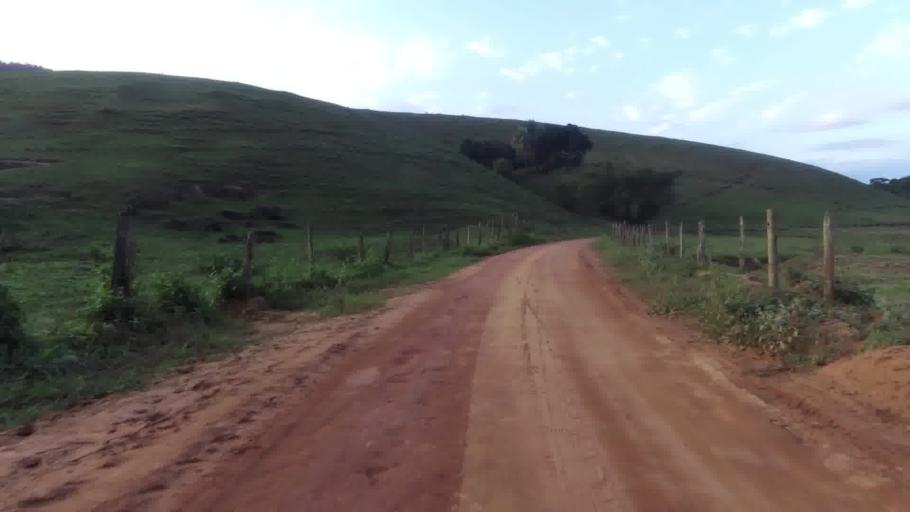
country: BR
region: Espirito Santo
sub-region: Alfredo Chaves
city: Alfredo Chaves
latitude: -20.6909
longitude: -40.6311
